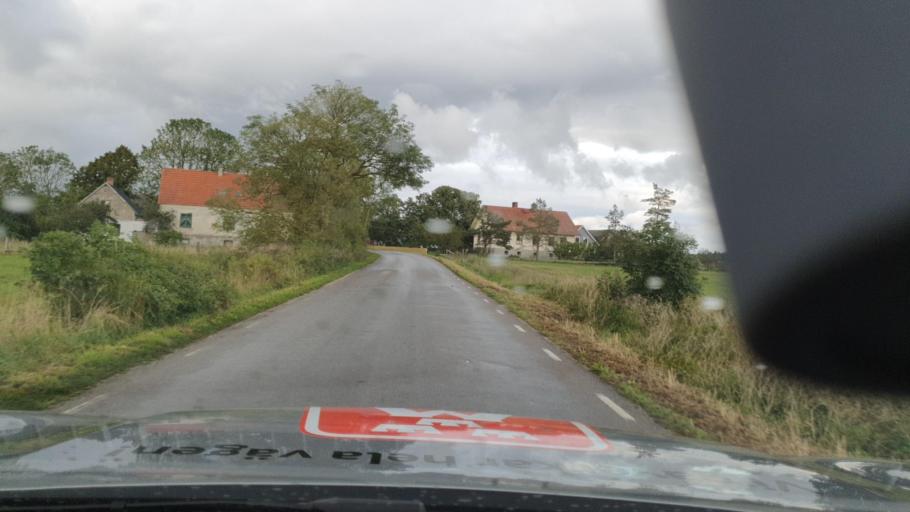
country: SE
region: Gotland
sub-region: Gotland
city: Vibble
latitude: 57.5054
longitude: 18.2071
